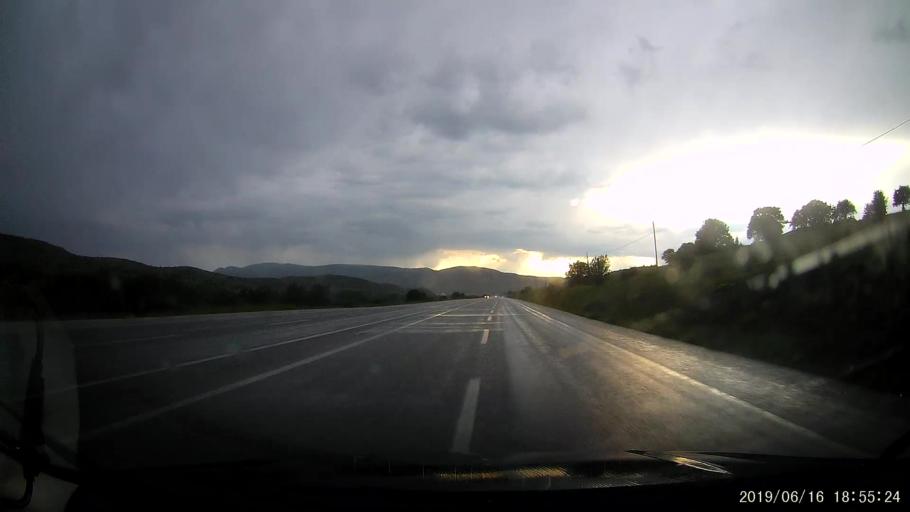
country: TR
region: Erzincan
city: Refahiye
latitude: 39.8999
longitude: 38.8290
